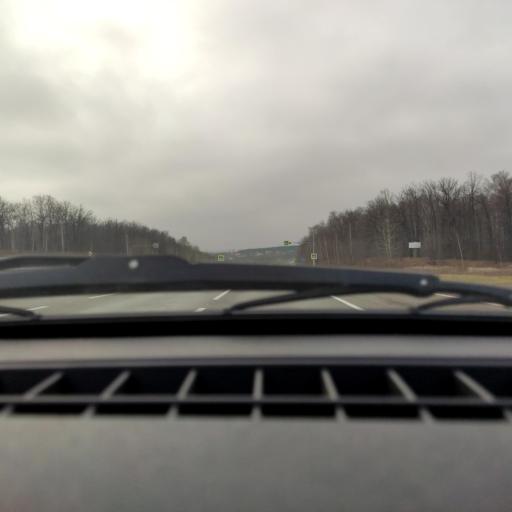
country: RU
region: Bashkortostan
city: Avdon
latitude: 54.6408
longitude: 55.6084
